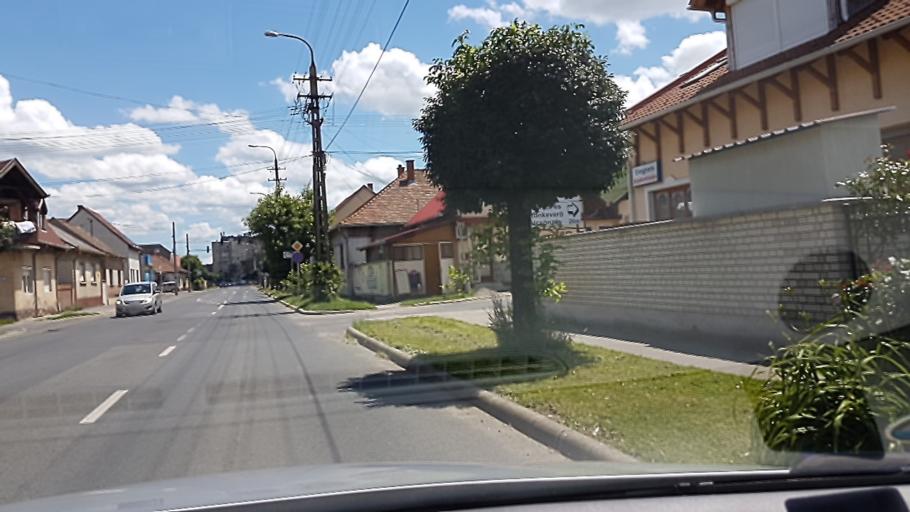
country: HU
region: Zala
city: Zalaegerszeg
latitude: 46.8495
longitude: 16.8218
